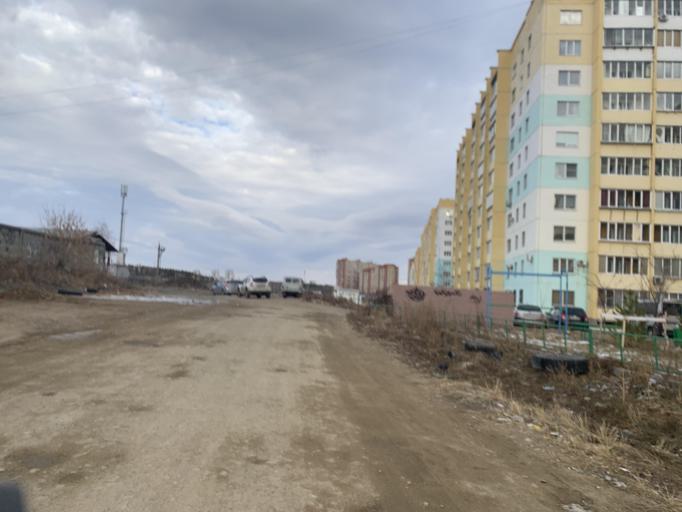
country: RU
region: Chelyabinsk
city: Roshchino
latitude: 55.1899
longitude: 61.2709
